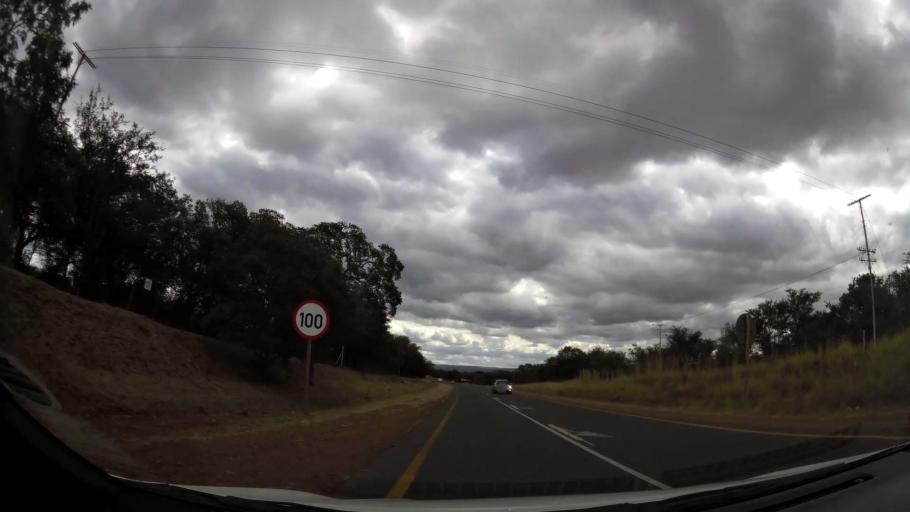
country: ZA
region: Limpopo
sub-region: Waterberg District Municipality
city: Modimolle
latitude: -24.7739
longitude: 28.4713
